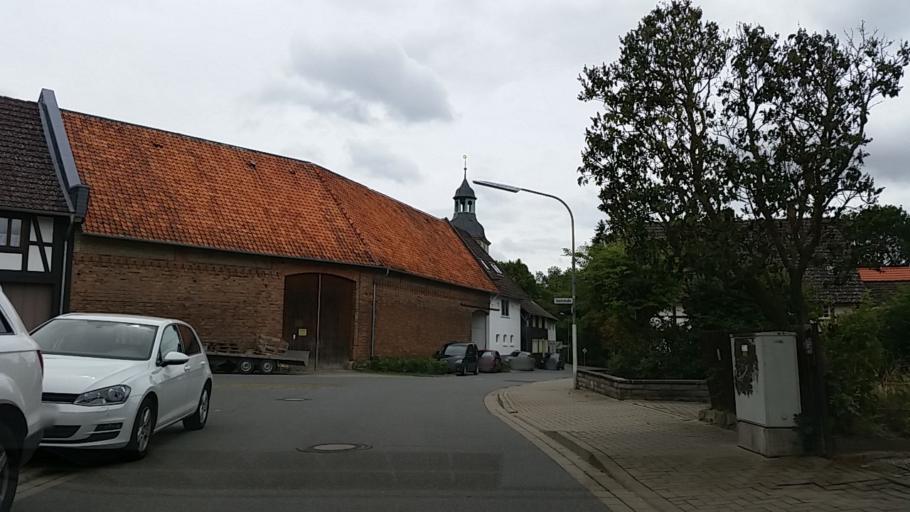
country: DE
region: Lower Saxony
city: Vienenburg
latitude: 51.9485
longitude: 10.5657
